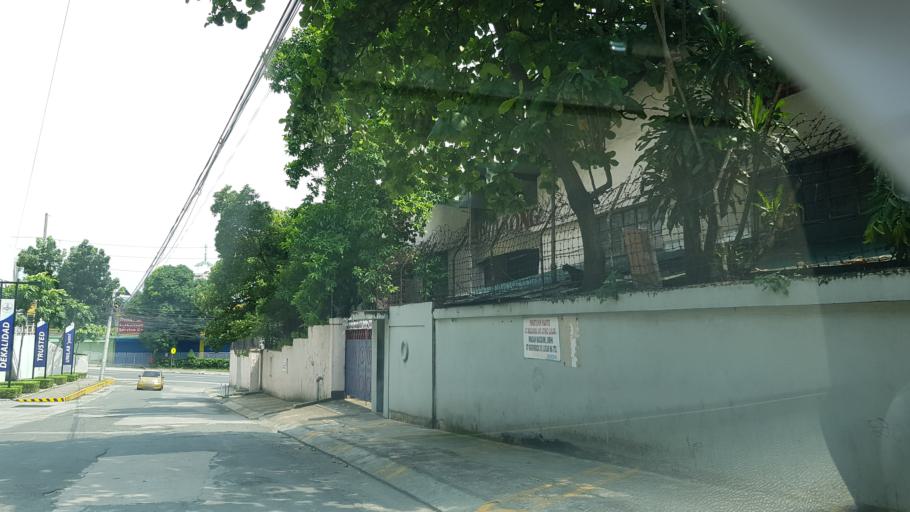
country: PH
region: Metro Manila
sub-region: Pasig
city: Pasig City
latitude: 14.5740
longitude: 121.0561
